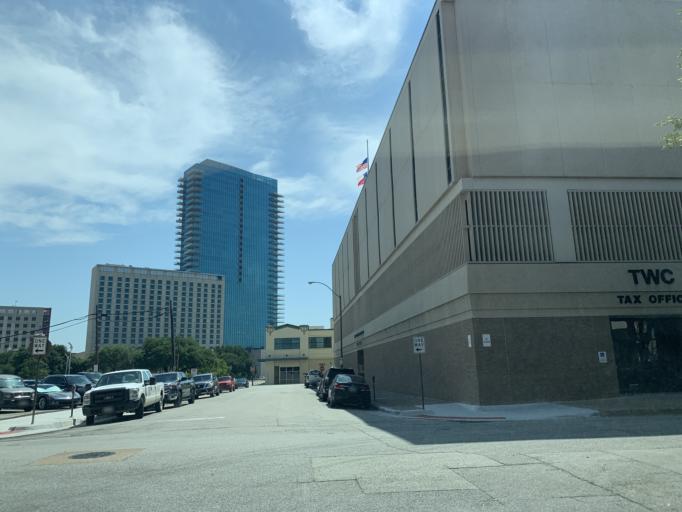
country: US
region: Texas
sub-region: Tarrant County
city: Fort Worth
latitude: 32.7478
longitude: -97.3321
